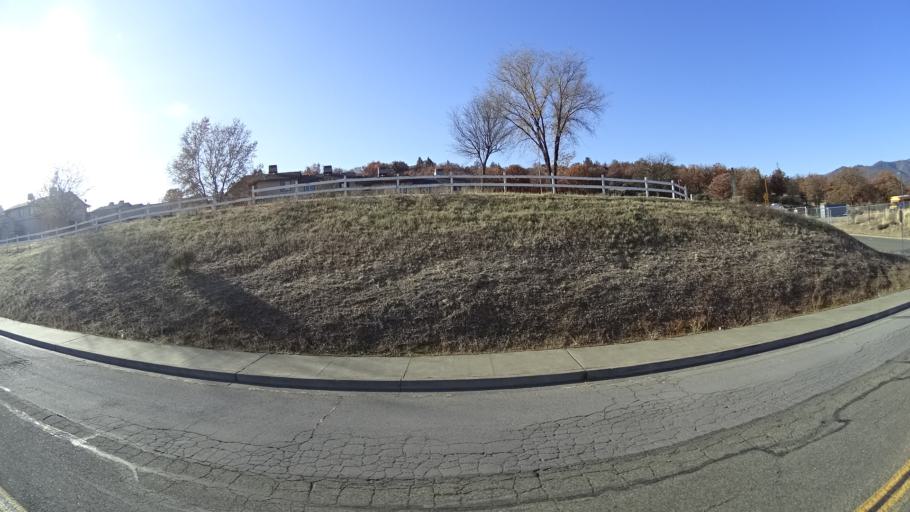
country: US
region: California
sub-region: Siskiyou County
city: Yreka
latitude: 41.7143
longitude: -122.6272
